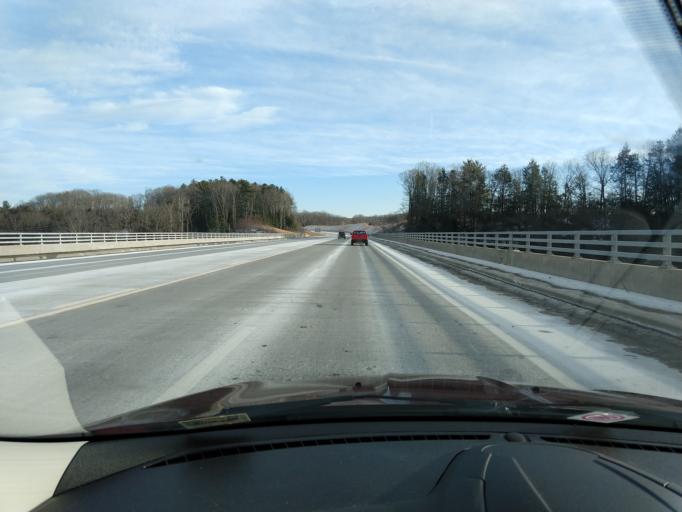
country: US
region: West Virginia
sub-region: Raleigh County
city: Stanaford
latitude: 37.7872
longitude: -81.1575
